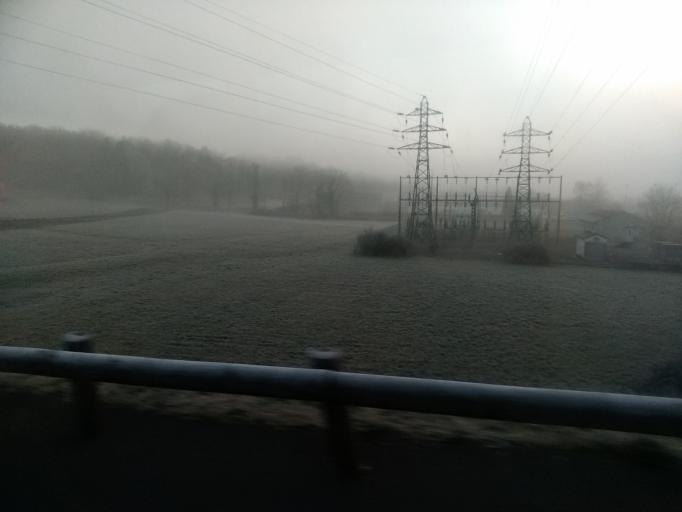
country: FR
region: Aquitaine
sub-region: Departement de la Dordogne
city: Terrasson-Lavilledieu
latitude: 45.1332
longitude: 1.2743
